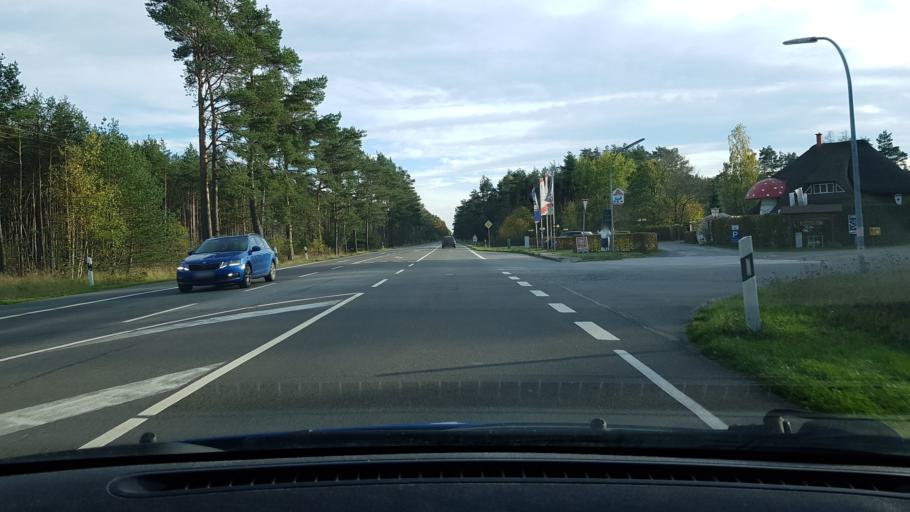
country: DE
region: Lower Saxony
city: Wagenhoff
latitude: 52.5708
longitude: 10.5035
